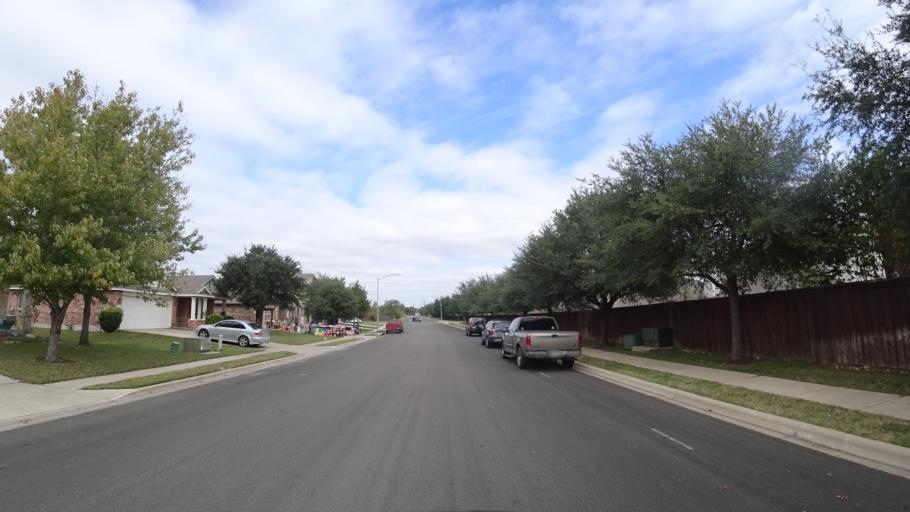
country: US
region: Texas
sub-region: Travis County
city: Manchaca
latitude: 30.1465
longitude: -97.8426
